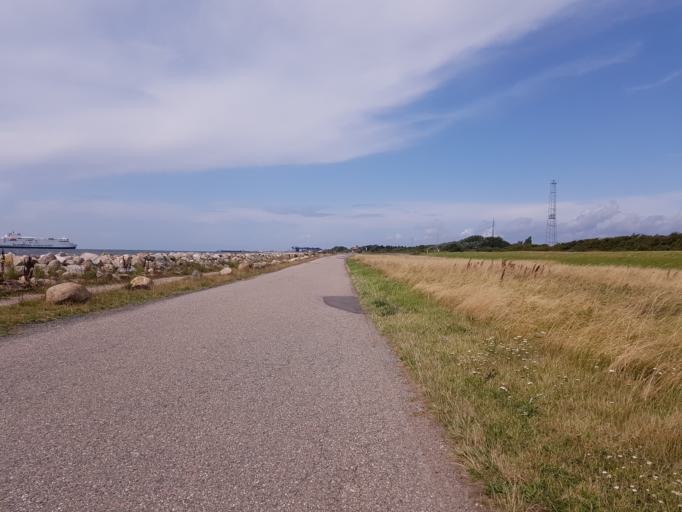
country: DK
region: Zealand
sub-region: Guldborgsund Kommune
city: Nykobing Falster
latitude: 54.5671
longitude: 11.9466
